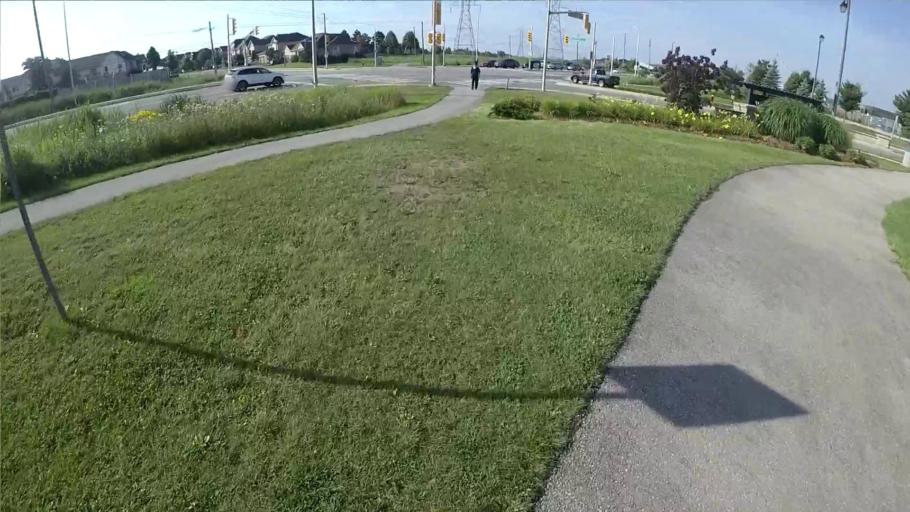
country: CA
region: Ontario
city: Burlington
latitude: 43.4019
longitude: -79.8142
